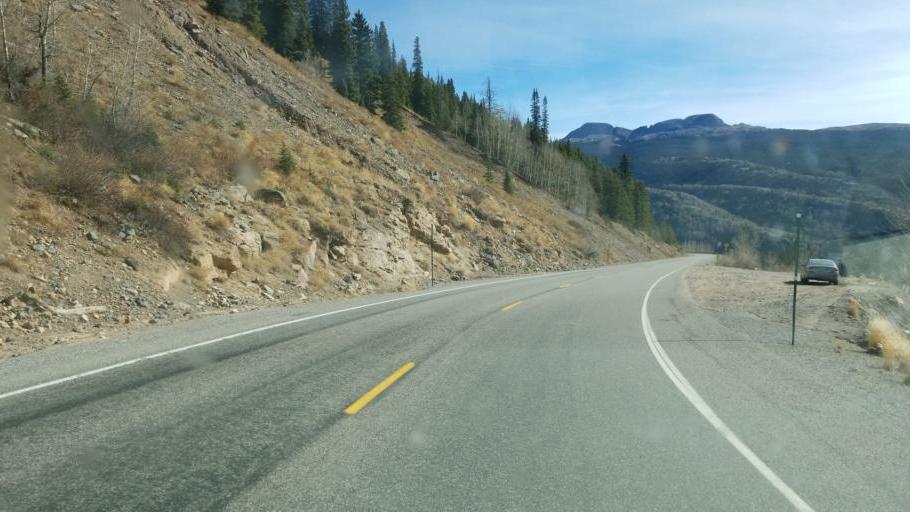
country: US
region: Colorado
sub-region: San Juan County
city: Silverton
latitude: 37.7086
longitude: -107.7708
